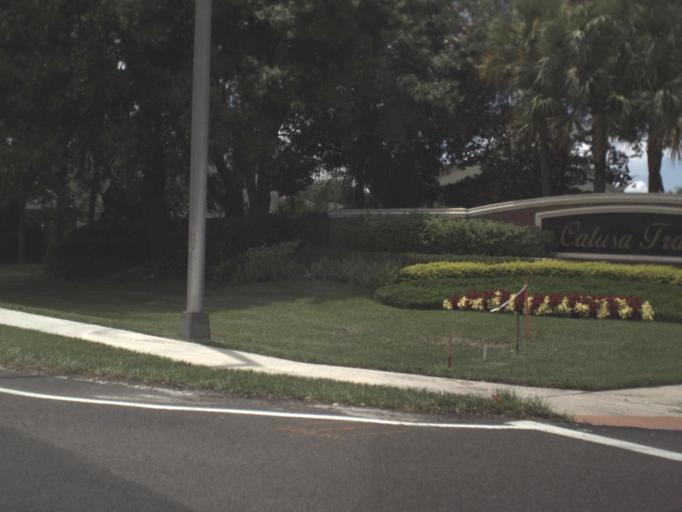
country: US
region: Florida
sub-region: Hillsborough County
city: Cheval
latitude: 28.1384
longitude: -82.5009
